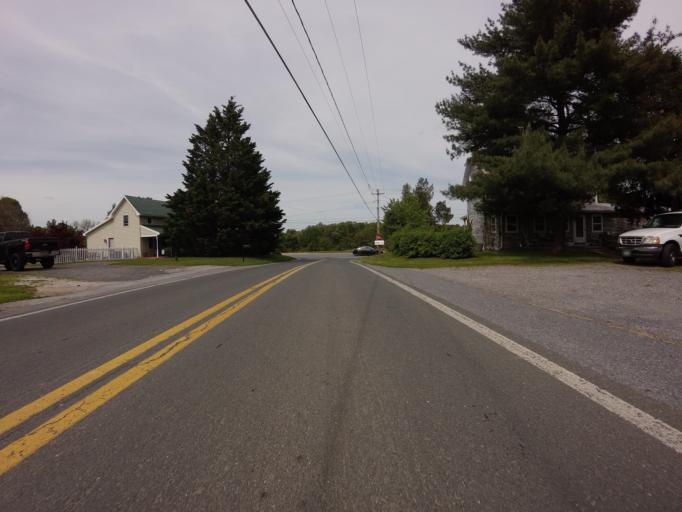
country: US
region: Maryland
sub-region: Carroll County
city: Eldersburg
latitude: 39.4727
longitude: -76.9507
